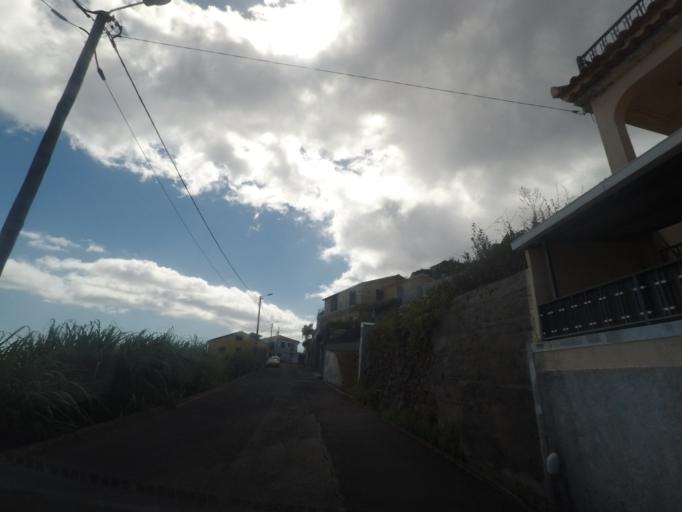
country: PT
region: Madeira
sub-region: Ribeira Brava
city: Campanario
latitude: 32.6736
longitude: -17.0514
